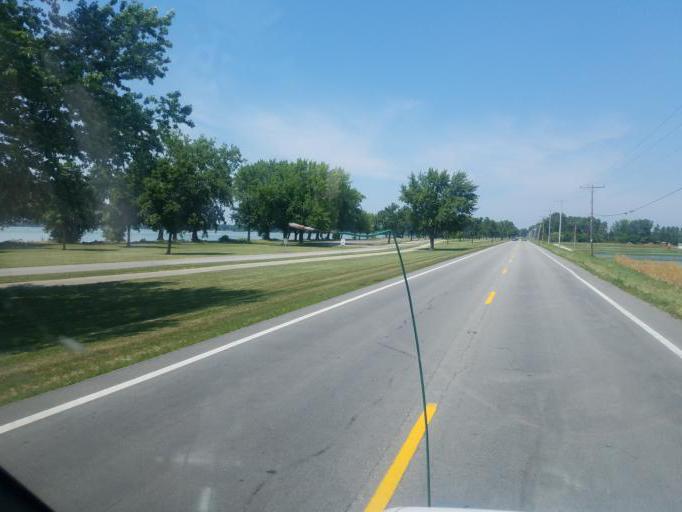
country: US
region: Ohio
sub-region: Auglaize County
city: Saint Marys
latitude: 40.5263
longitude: -84.4201
